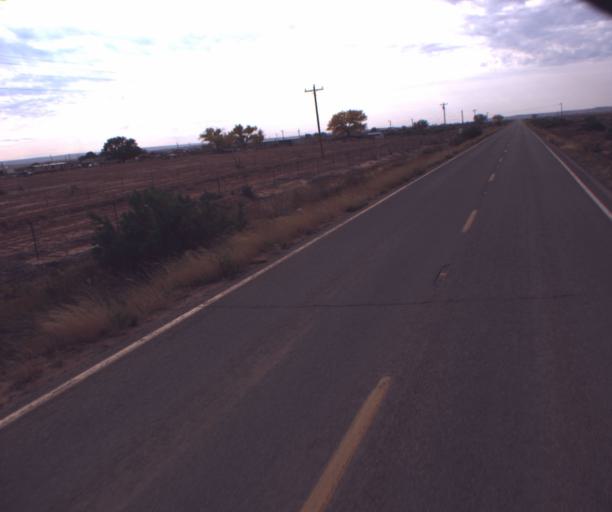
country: US
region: Arizona
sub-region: Apache County
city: Many Farms
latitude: 36.4123
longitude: -109.6074
